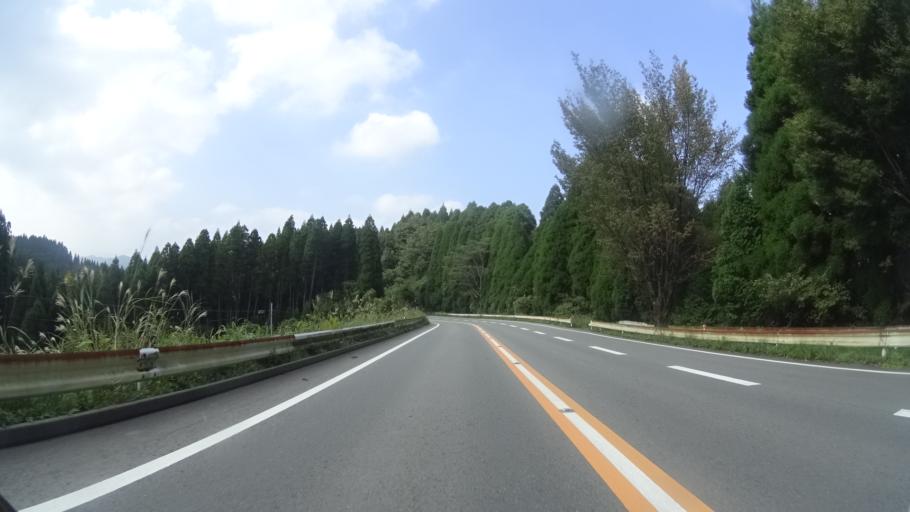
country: JP
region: Kumamoto
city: Aso
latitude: 33.0671
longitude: 131.0667
